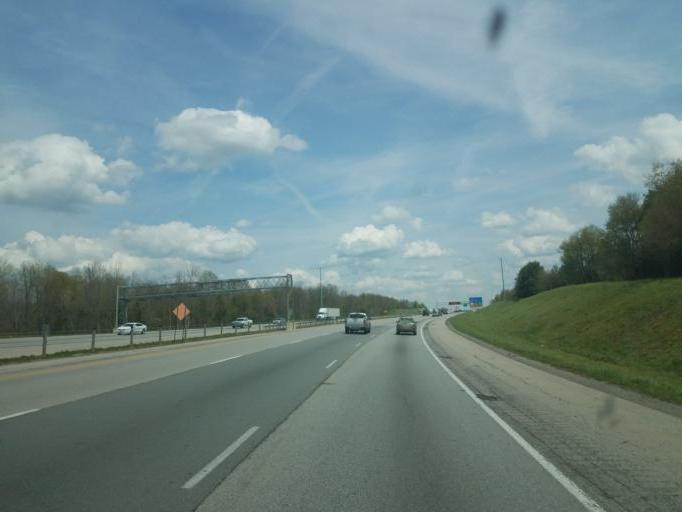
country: US
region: Kentucky
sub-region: Hardin County
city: Elizabethtown
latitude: 37.6898
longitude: -85.8424
